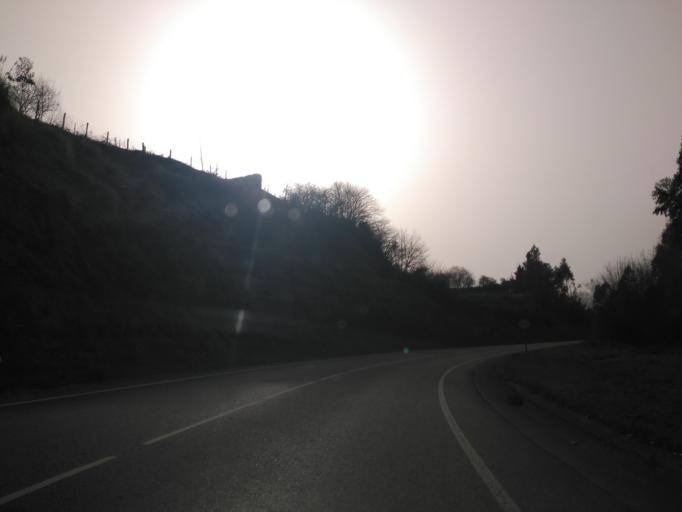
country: ES
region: Cantabria
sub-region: Provincia de Cantabria
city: Cabezon de la Sal
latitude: 43.3395
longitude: -4.2714
